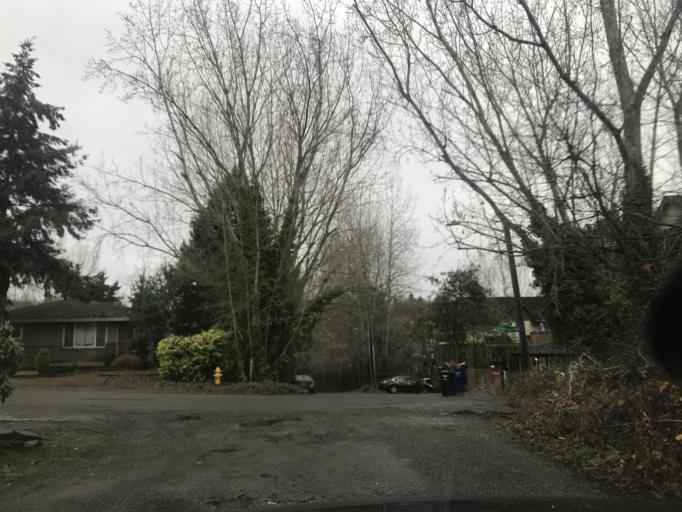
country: US
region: Washington
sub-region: King County
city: White Center
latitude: 47.5301
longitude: -122.3615
